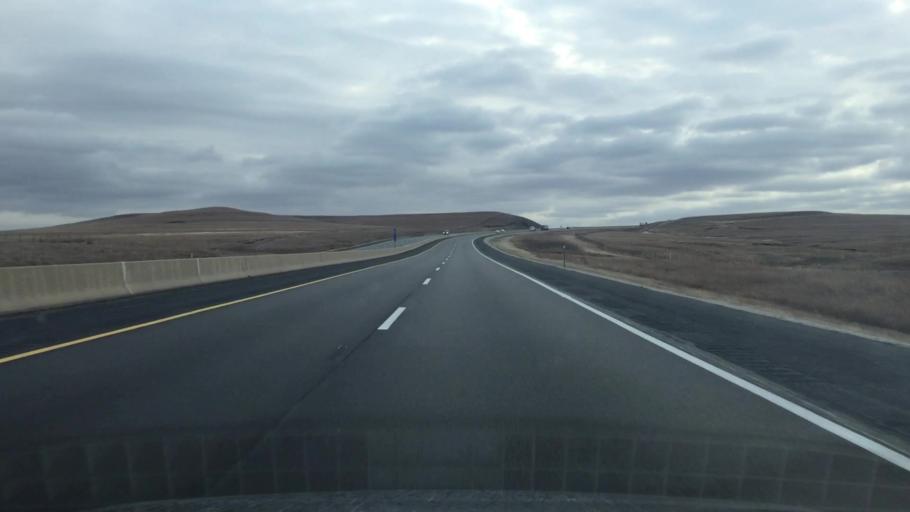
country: US
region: Kansas
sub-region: Chase County
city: Cottonwood Falls
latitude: 38.2454
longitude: -96.3941
